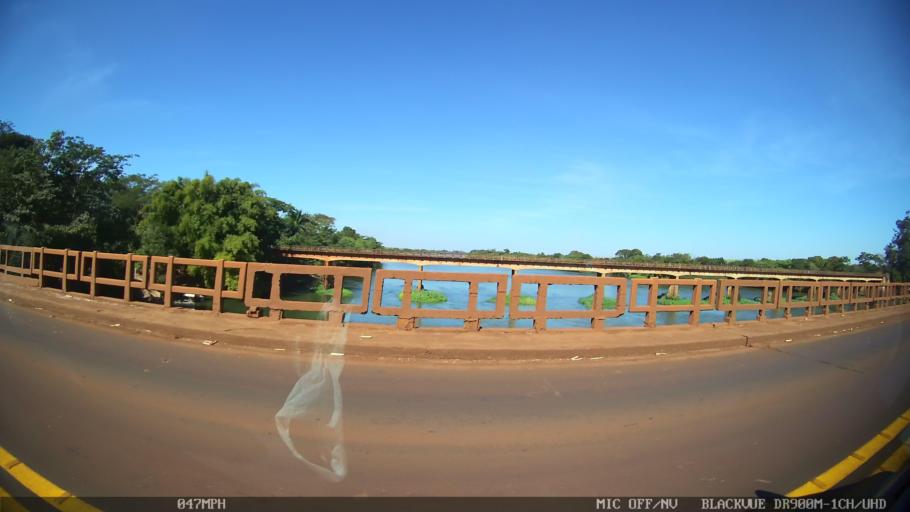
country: BR
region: Sao Paulo
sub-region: Barretos
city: Barretos
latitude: -20.4516
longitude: -48.4554
